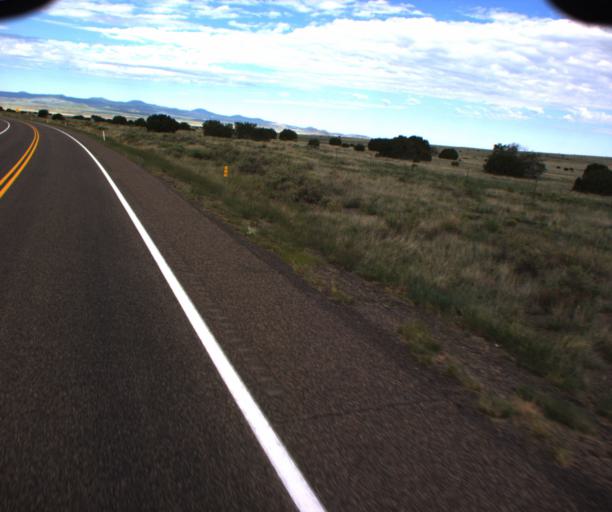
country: US
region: Arizona
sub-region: Apache County
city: Springerville
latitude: 34.1457
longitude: -109.2191
